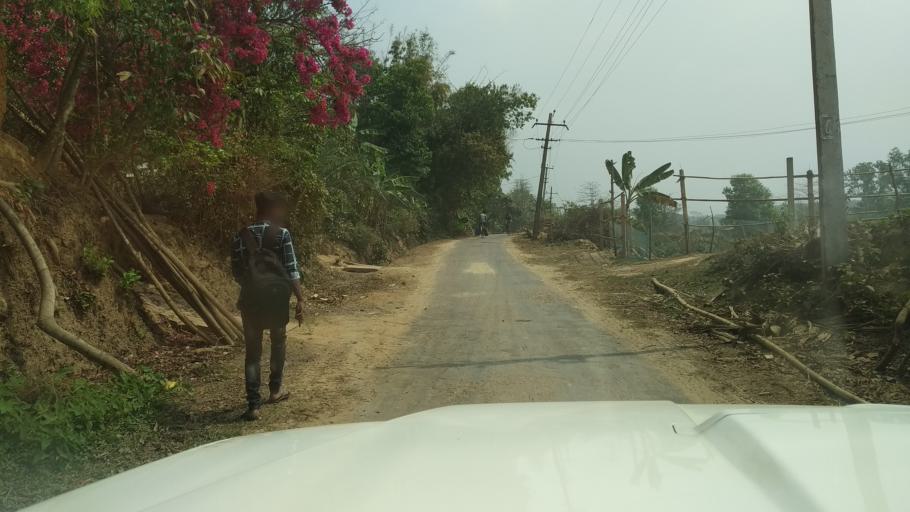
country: IN
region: Tripura
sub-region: West Tripura
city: Sonamura
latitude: 23.4238
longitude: 91.2965
